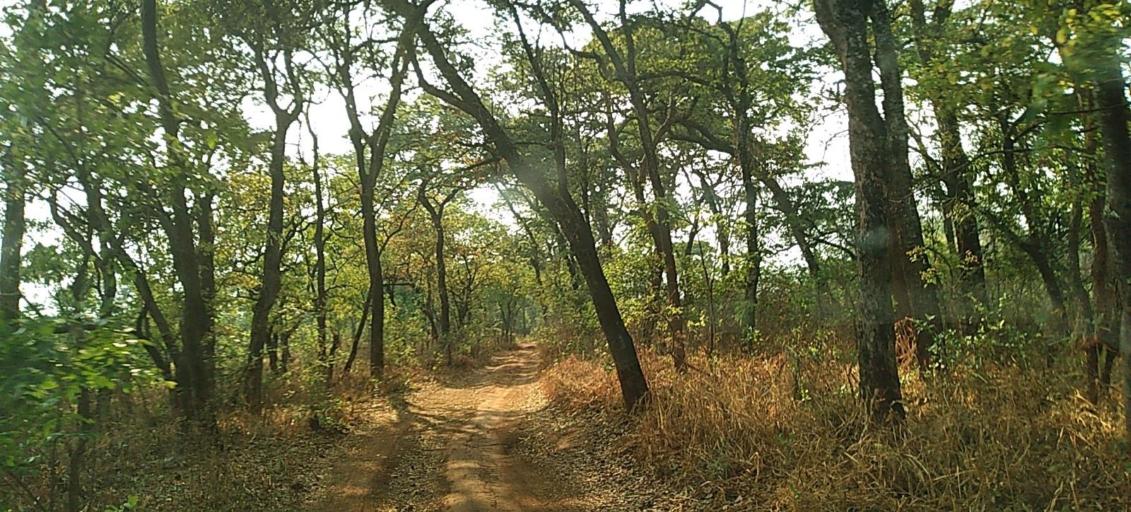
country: ZM
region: North-Western
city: Solwezi
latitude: -12.0586
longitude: 26.1635
